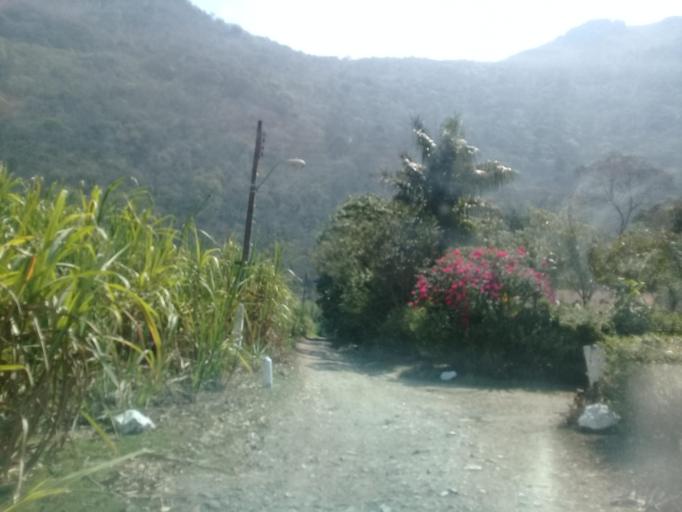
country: MX
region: Veracruz
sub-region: Ixtaczoquitlan
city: Capoluca
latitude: 18.8055
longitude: -96.9856
